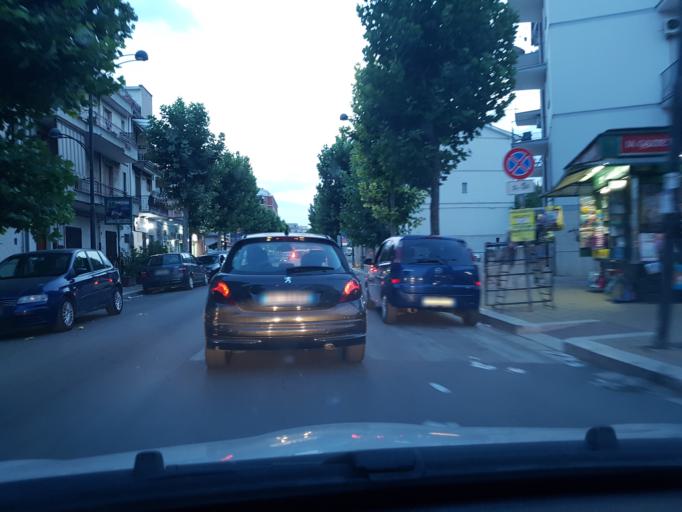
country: IT
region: Apulia
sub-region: Provincia di Foggia
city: Cerignola
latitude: 41.2604
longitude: 15.9020
